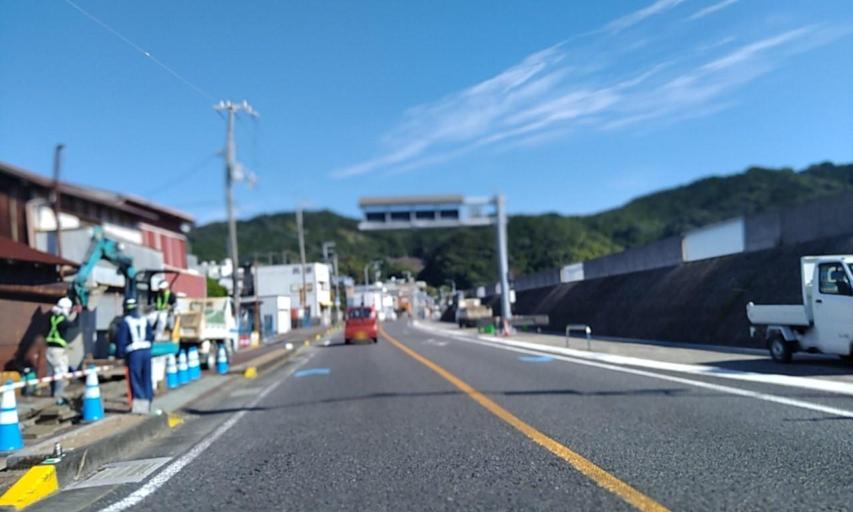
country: JP
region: Wakayama
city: Shingu
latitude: 33.8896
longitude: 136.1042
